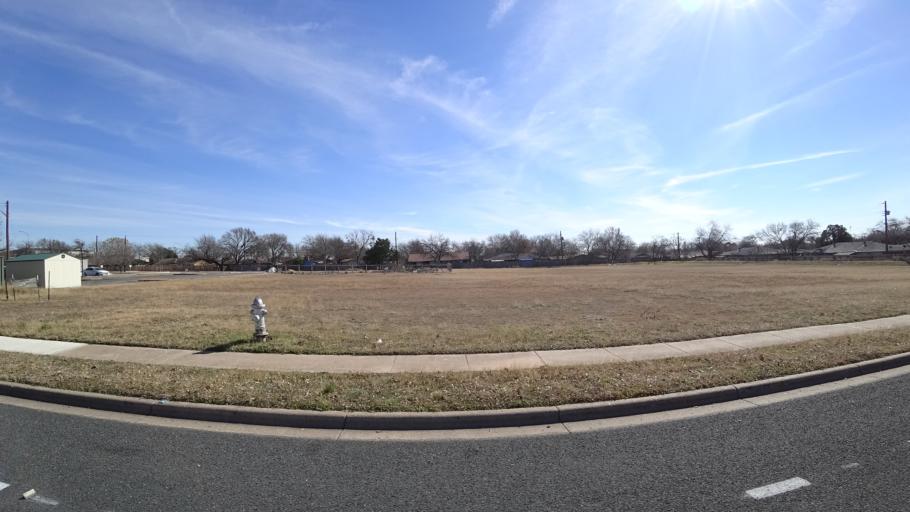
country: US
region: Texas
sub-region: Travis County
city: Wells Branch
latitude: 30.3847
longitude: -97.6967
